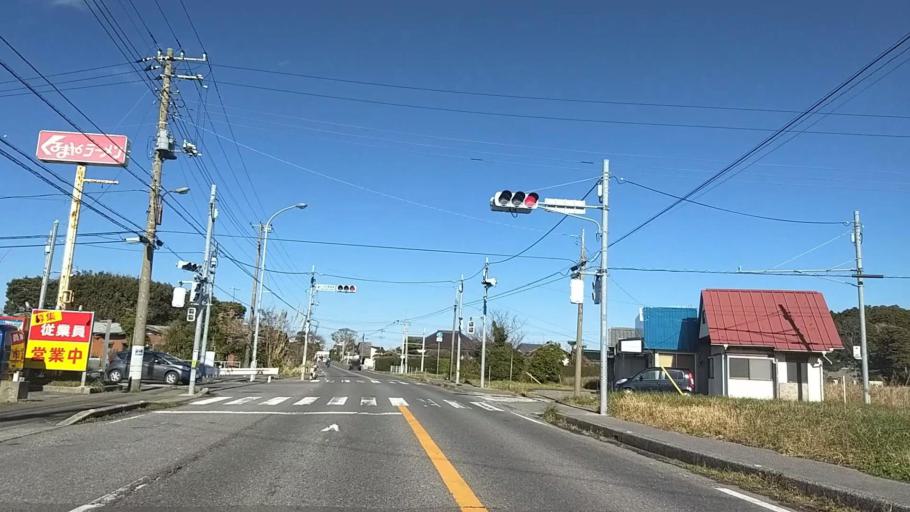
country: JP
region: Chiba
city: Ohara
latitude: 35.2425
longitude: 140.3927
